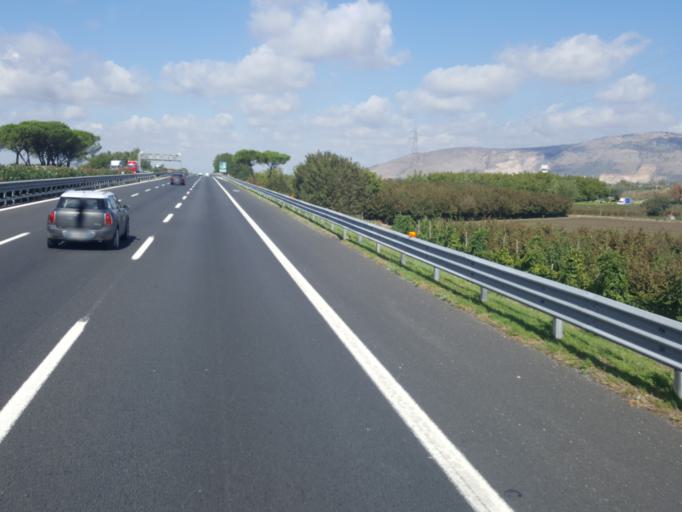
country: IT
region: Campania
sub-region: Provincia di Napoli
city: San Vitaliano
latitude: 40.9464
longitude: 14.4821
